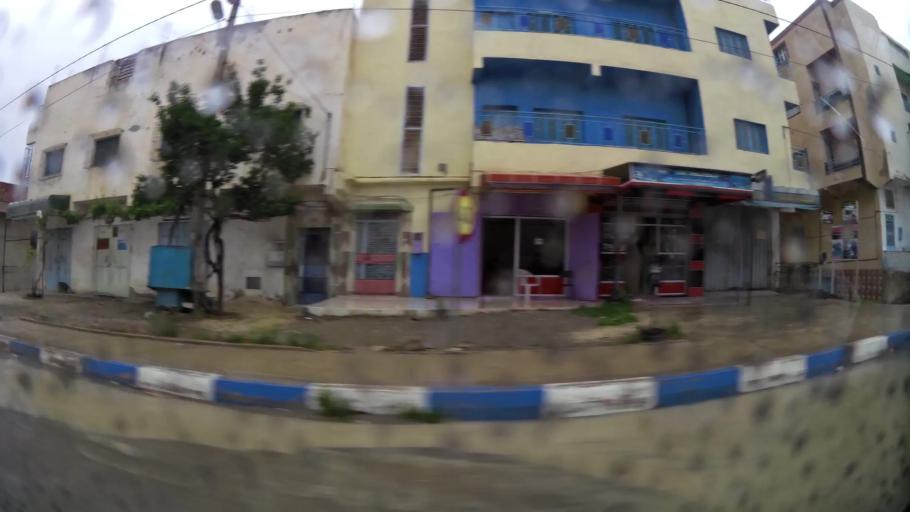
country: MA
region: Oriental
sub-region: Nador
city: Midar
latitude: 34.8876
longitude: -3.7273
